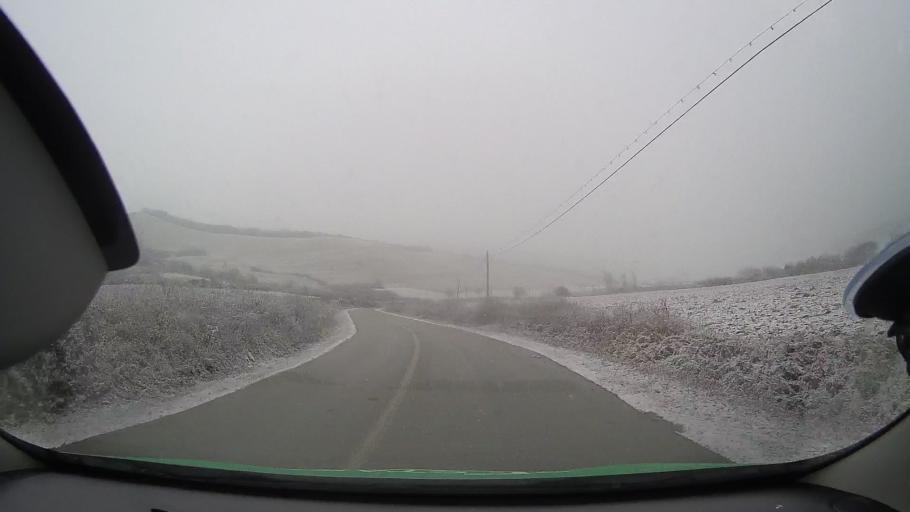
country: RO
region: Alba
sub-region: Comuna Lopadea Noua
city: Lopadea Noua
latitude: 46.2962
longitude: 23.8427
